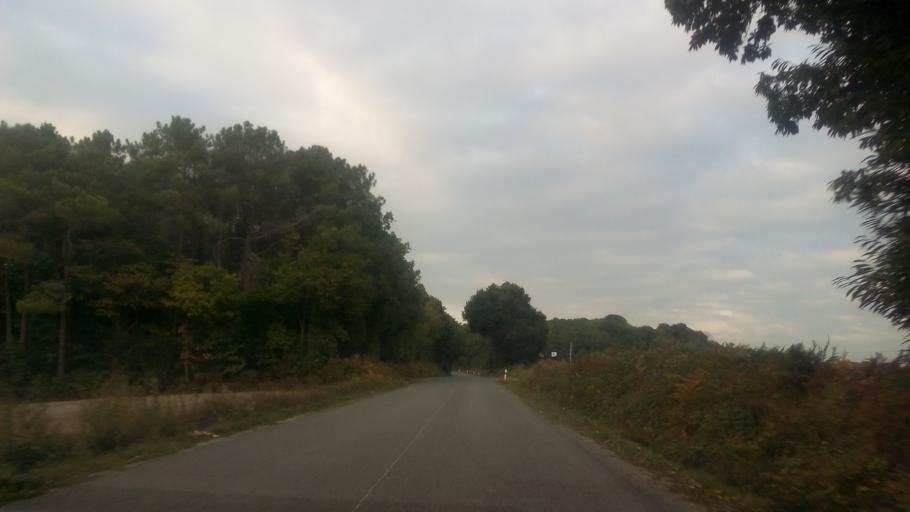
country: FR
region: Brittany
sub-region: Departement du Morbihan
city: Saint-Jacut-les-Pins
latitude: 47.6996
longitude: -2.2143
